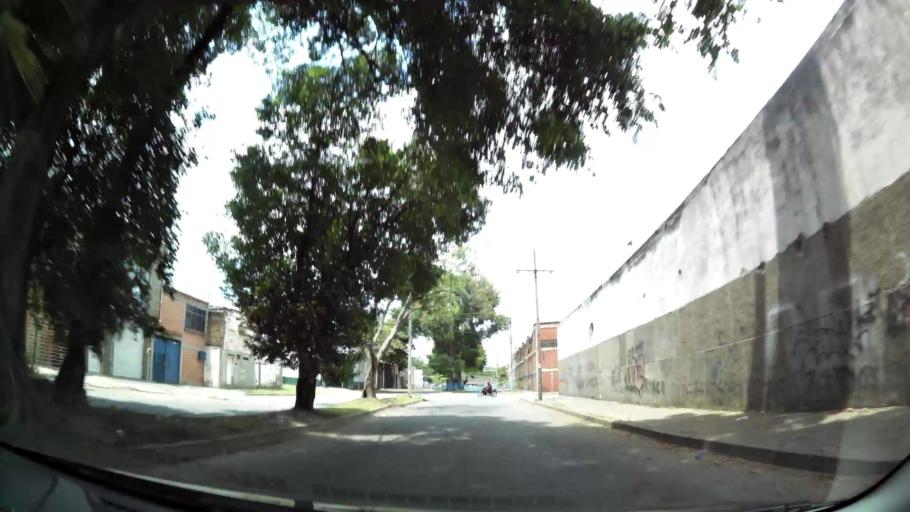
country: CO
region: Valle del Cauca
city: Cali
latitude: 3.4524
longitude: -76.5073
